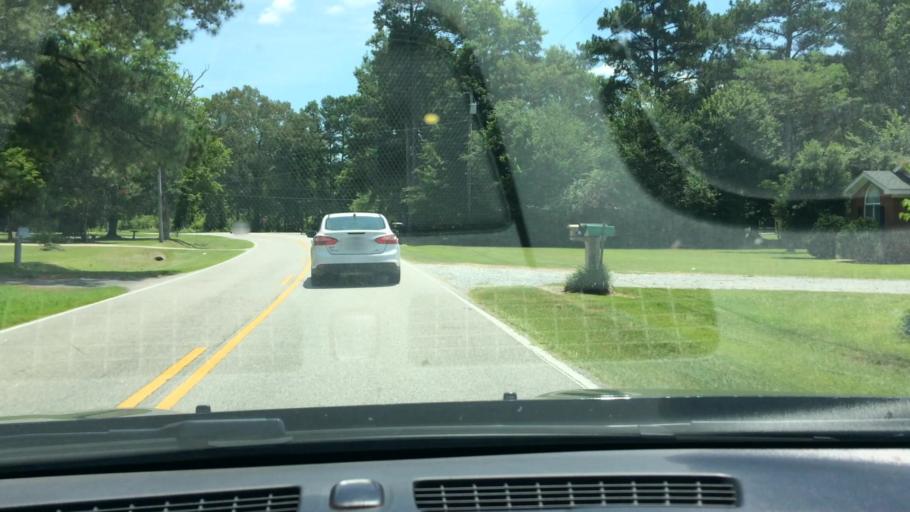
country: US
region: North Carolina
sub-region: Pitt County
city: Windsor
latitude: 35.5663
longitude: -77.2102
